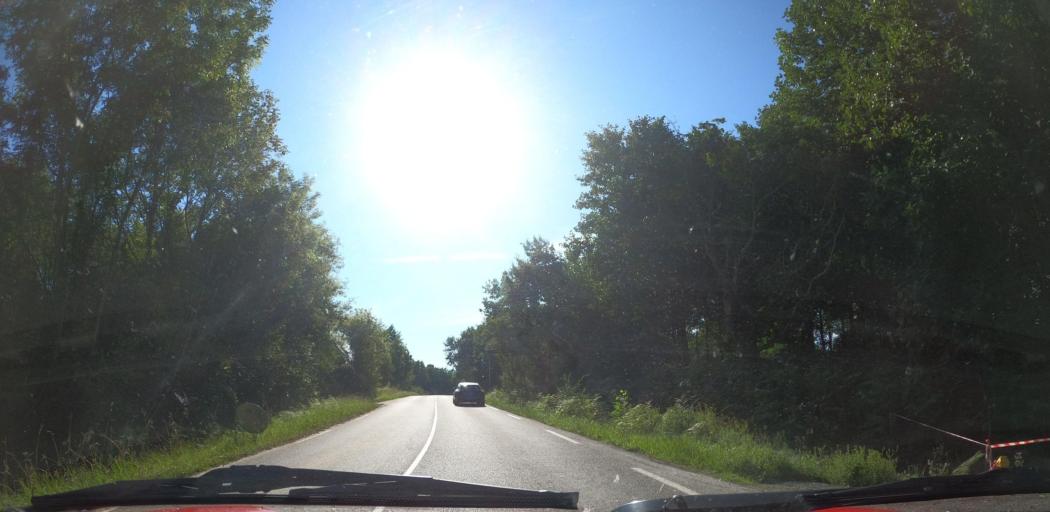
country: FR
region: Aquitaine
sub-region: Departement des Pyrenees-Atlantiques
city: Saint-Pee-sur-Nivelle
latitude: 43.3822
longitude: -1.5413
